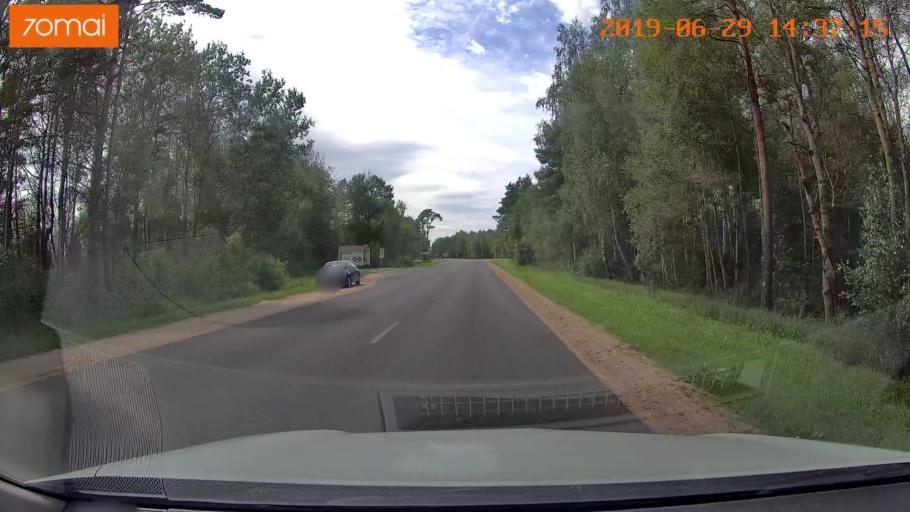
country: BY
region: Minsk
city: Starobin
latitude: 52.7506
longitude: 27.4682
